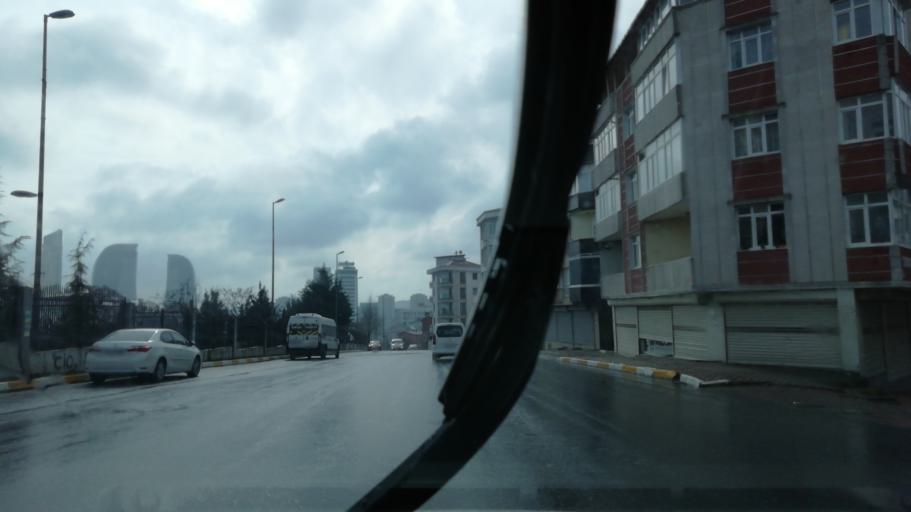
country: TR
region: Istanbul
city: Esenyurt
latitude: 41.0256
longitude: 28.6822
